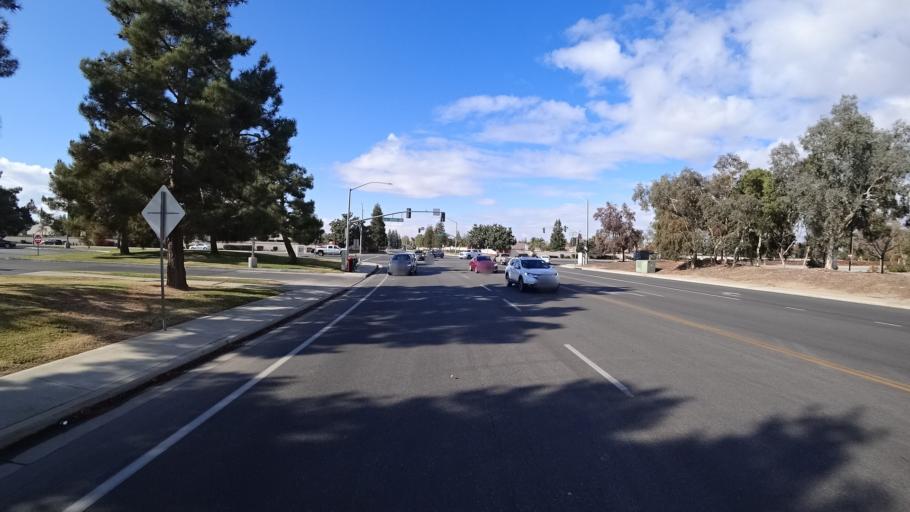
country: US
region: California
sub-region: Kern County
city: Greenacres
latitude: 35.3444
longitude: -119.1136
